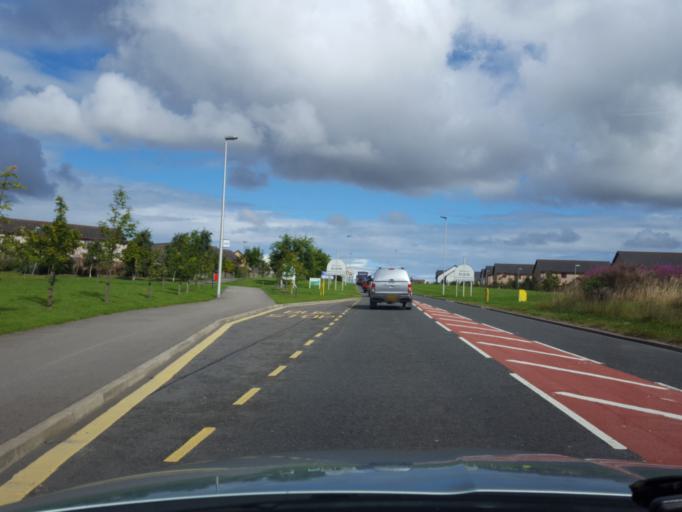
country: GB
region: Scotland
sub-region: Moray
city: Elgin
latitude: 57.6310
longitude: -3.3030
